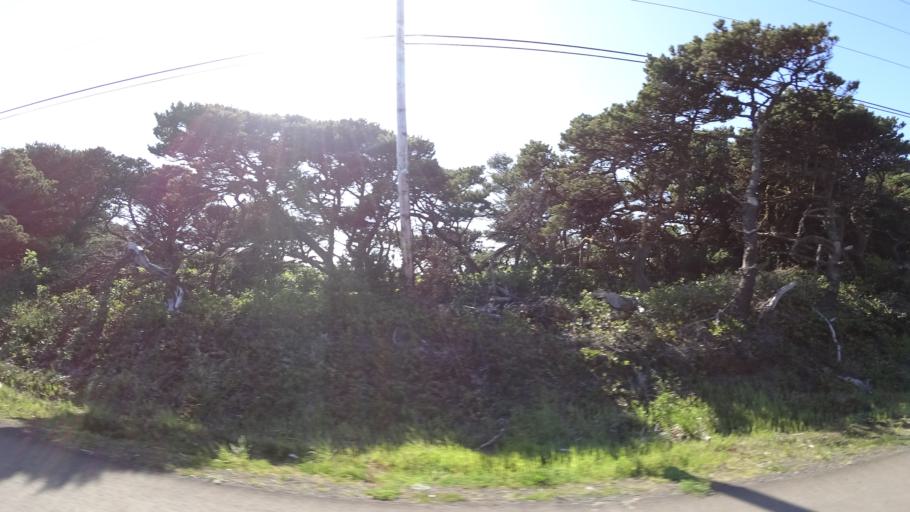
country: US
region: Oregon
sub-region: Lincoln County
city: Newport
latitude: 44.5418
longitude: -124.0737
